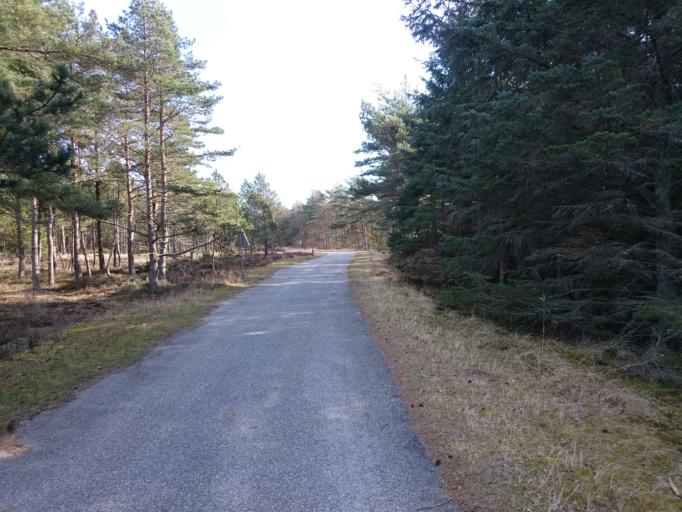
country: DK
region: North Denmark
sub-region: Frederikshavn Kommune
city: Skagen
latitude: 57.7034
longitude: 10.5128
